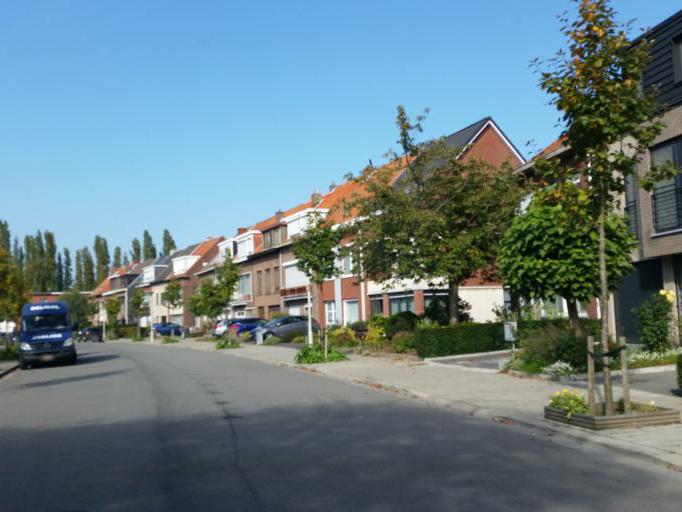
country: BE
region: Flanders
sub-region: Provincie Antwerpen
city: Aartselaar
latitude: 51.1534
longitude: 4.3879
